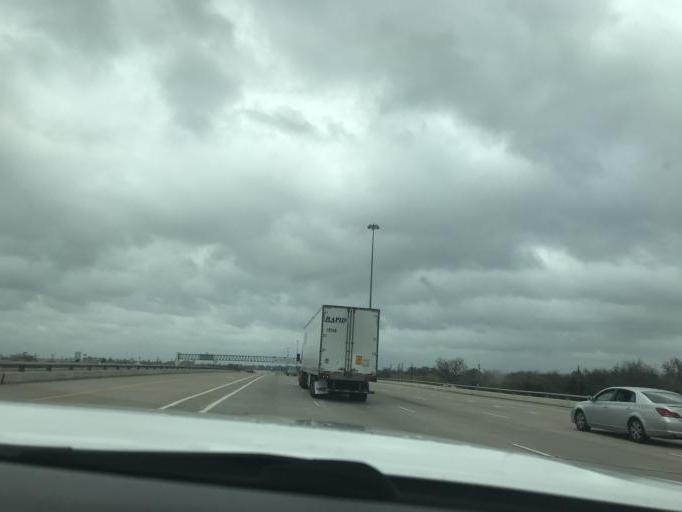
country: US
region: Texas
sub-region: Fort Bend County
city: Greatwood
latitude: 29.5611
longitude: -95.6907
